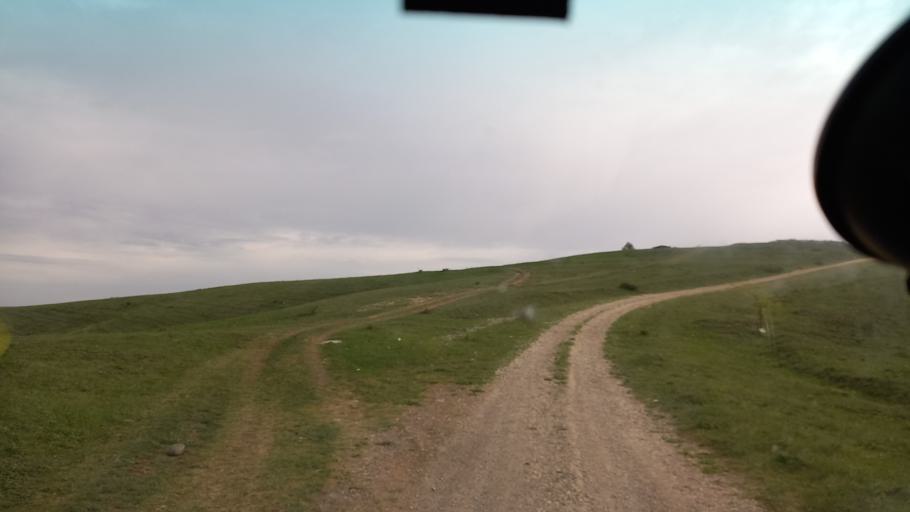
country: RU
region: Kabardino-Balkariya
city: Kuba-Taba
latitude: 43.8040
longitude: 43.3997
